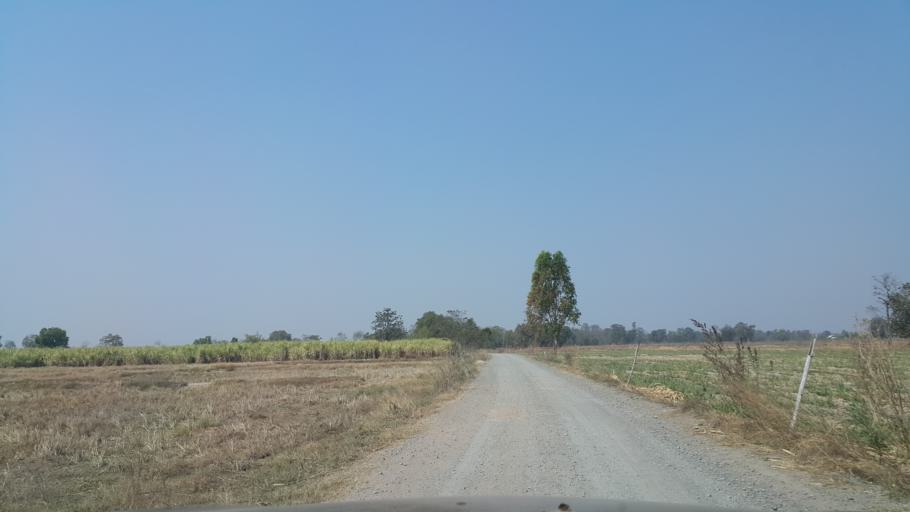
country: TH
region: Buriram
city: Krasang
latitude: 15.0908
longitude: 103.3804
